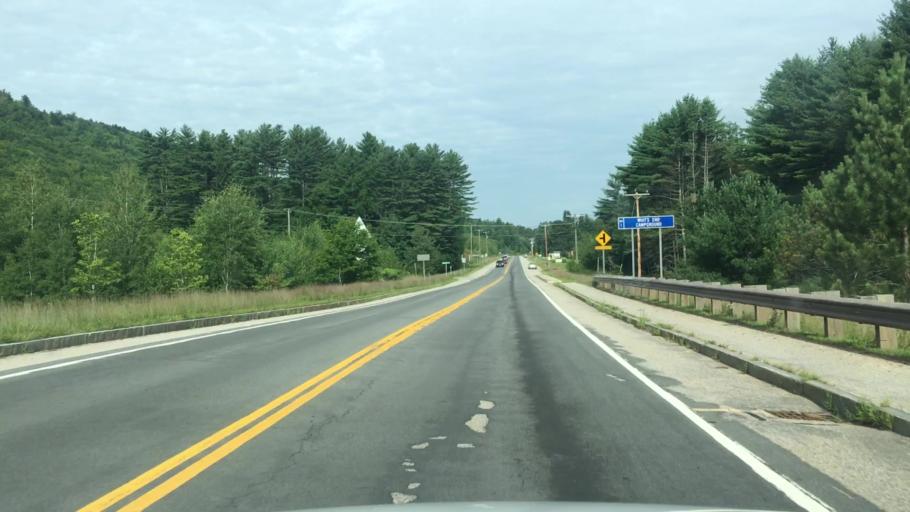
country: US
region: New Hampshire
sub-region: Carroll County
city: Tamworth
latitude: 43.8192
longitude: -71.2076
